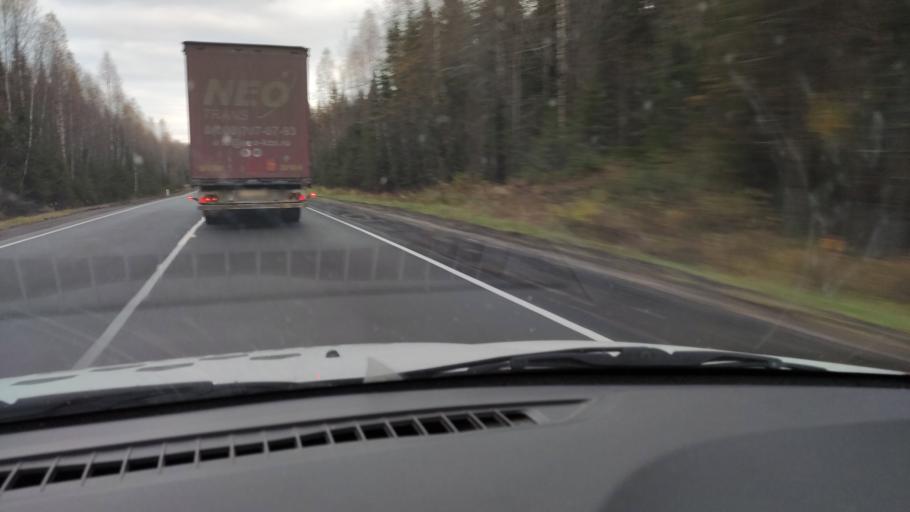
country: RU
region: Kirov
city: Omutninsk
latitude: 58.7605
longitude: 52.0104
